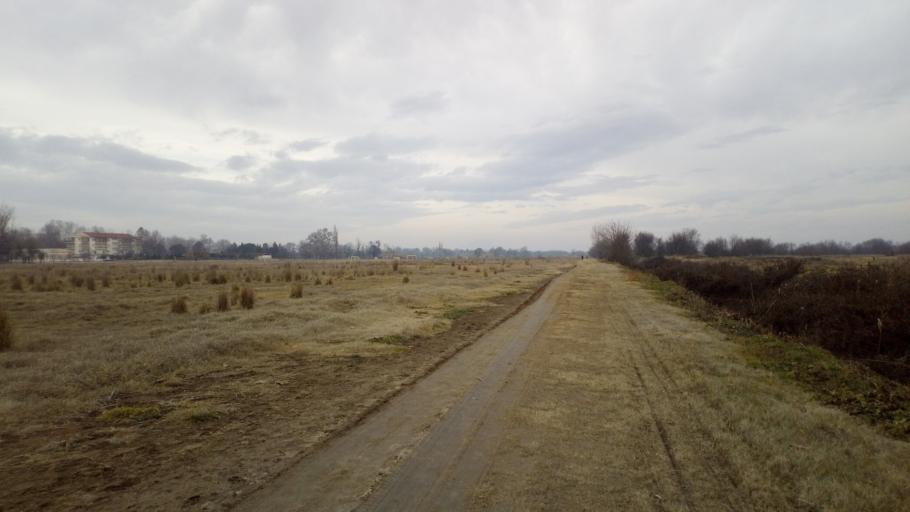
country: GR
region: Central Macedonia
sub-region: Nomos Thessalonikis
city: Lagkadas
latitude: 40.7321
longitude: 23.0914
